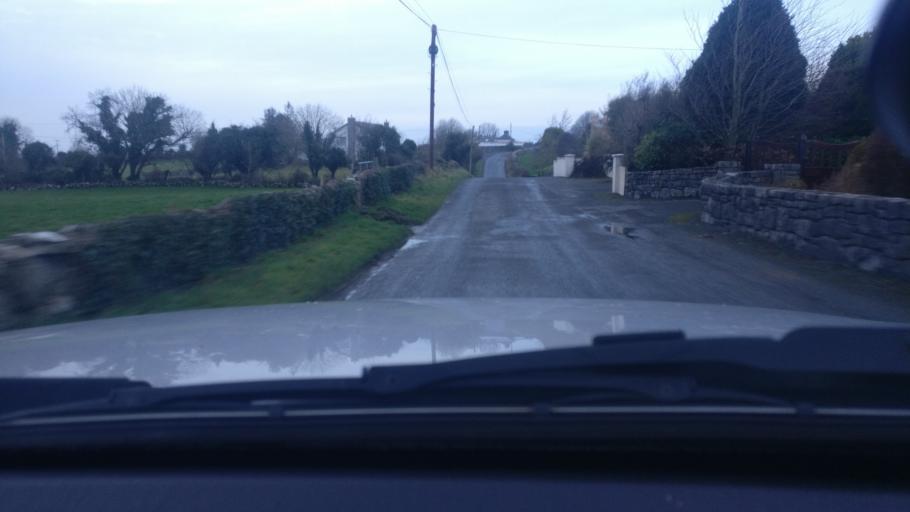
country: IE
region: Connaught
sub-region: County Galway
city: Loughrea
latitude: 53.1787
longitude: -8.5931
